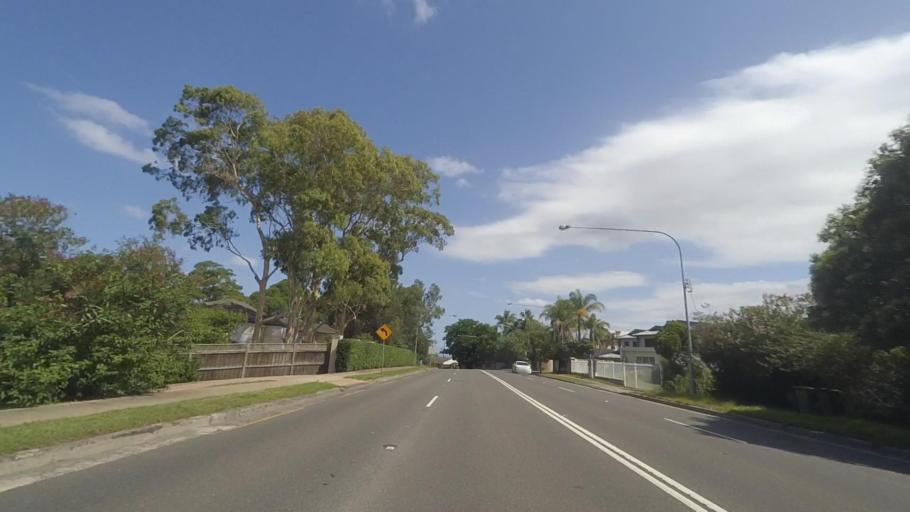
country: AU
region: New South Wales
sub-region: Parramatta
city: Dundas Valley
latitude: -33.7846
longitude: 151.0586
